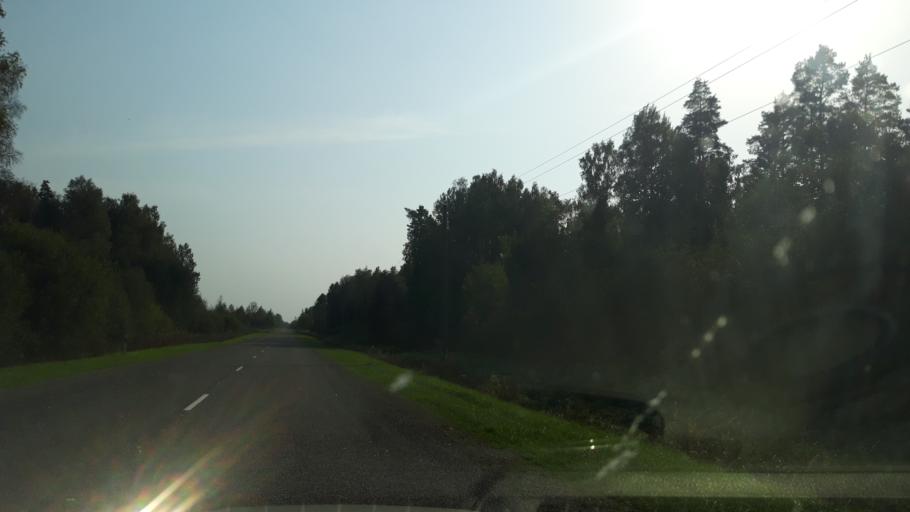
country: LV
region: Burtnieki
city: Matisi
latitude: 57.6431
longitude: 25.2464
